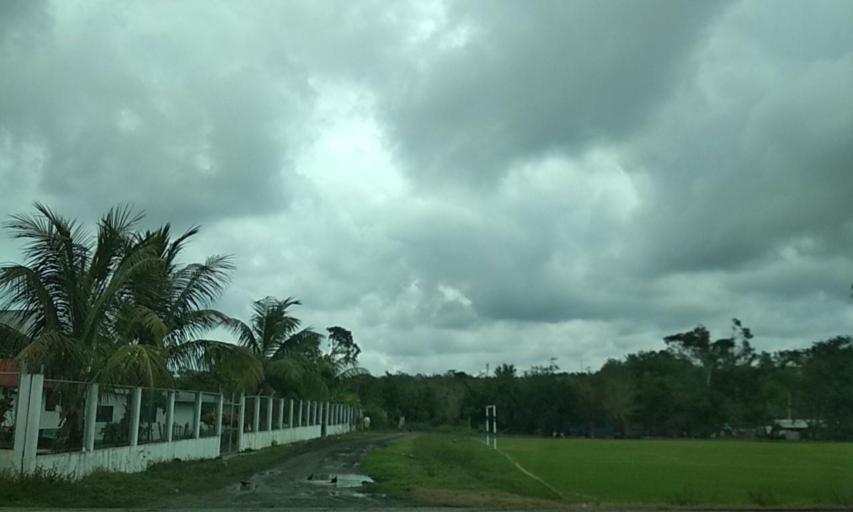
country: MX
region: Puebla
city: Espinal
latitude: 20.3249
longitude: -97.4185
